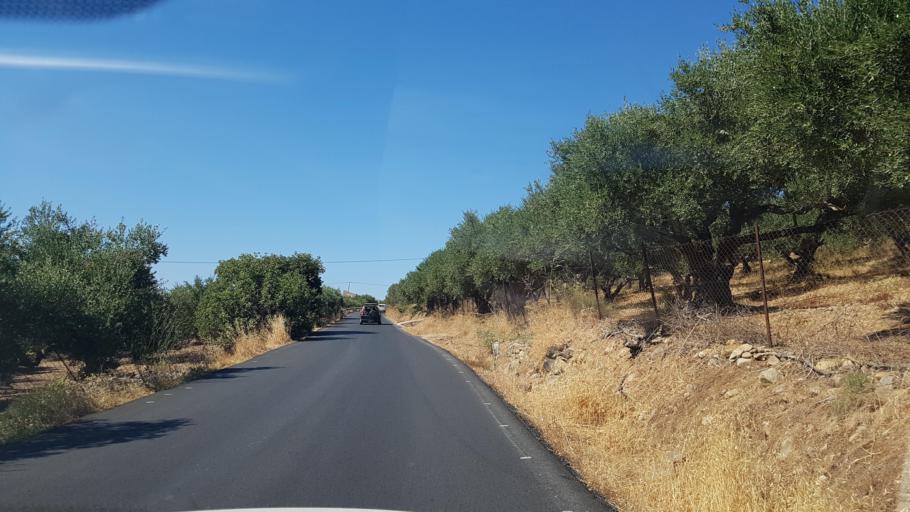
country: GR
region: Crete
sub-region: Nomos Chanias
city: Kissamos
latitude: 35.4889
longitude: 23.6915
